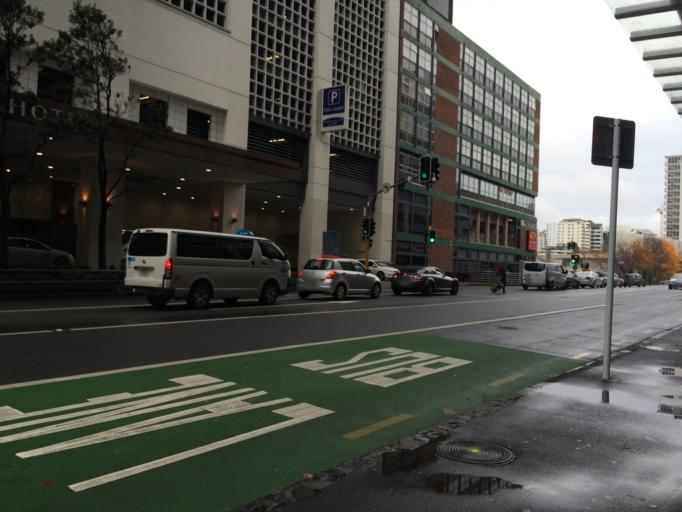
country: NZ
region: Auckland
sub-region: Auckland
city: Auckland
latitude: -36.8495
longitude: 174.7630
